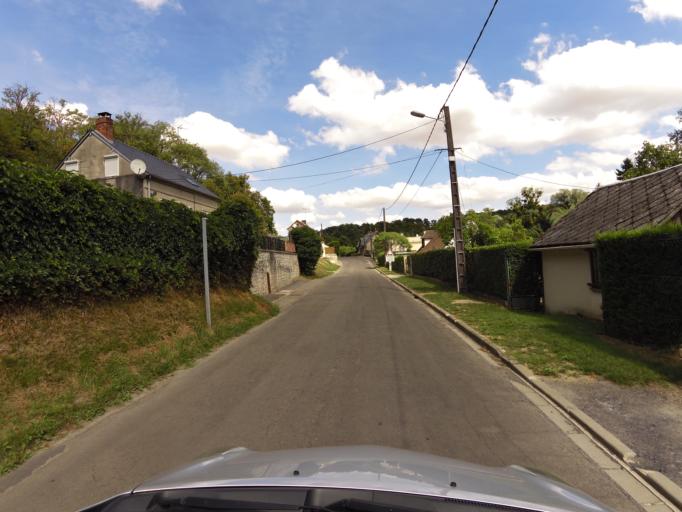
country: FR
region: Picardie
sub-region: Departement de l'Aisne
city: Neuilly-Saint-Front
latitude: 49.2544
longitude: 3.2148
